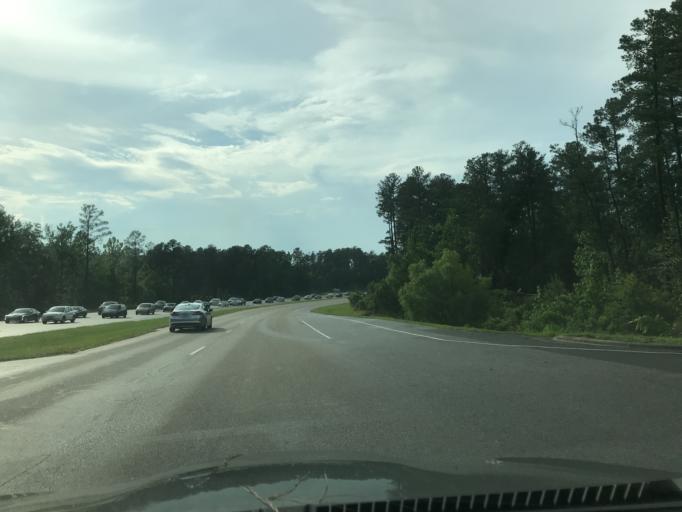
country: US
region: North Carolina
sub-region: Wake County
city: Morrisville
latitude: 35.8587
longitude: -78.8706
